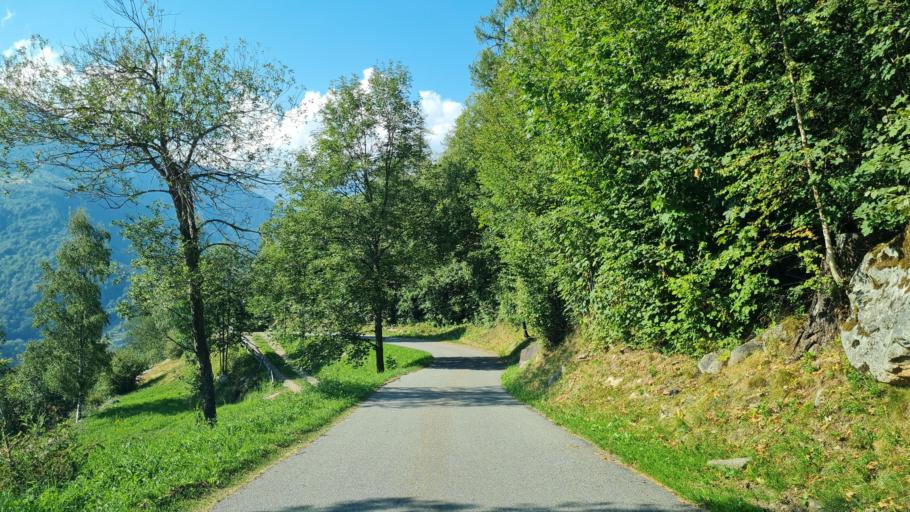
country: IT
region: Aosta Valley
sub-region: Valle d'Aosta
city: Fontainemore
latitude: 45.6310
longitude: 7.8601
